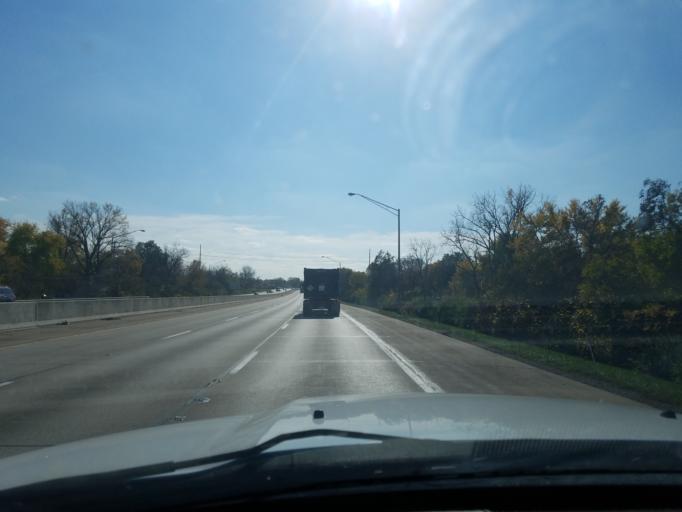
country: US
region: Indiana
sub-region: Marion County
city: Speedway
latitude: 39.7406
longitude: -86.2390
